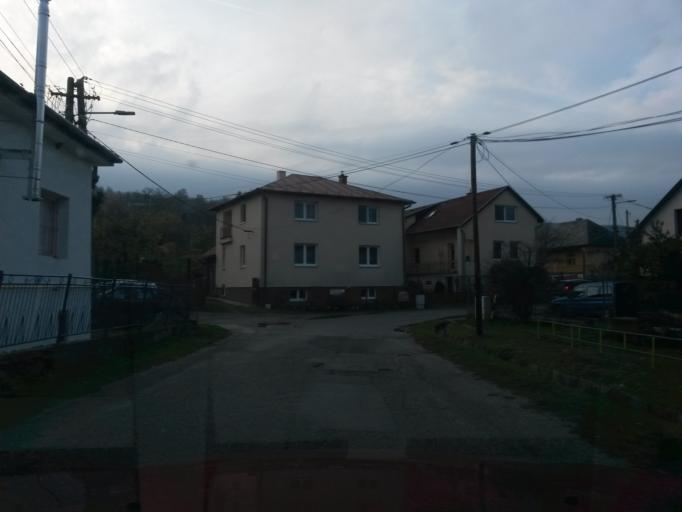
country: SK
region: Kosicky
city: Kosice
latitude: 48.7755
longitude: 21.2056
